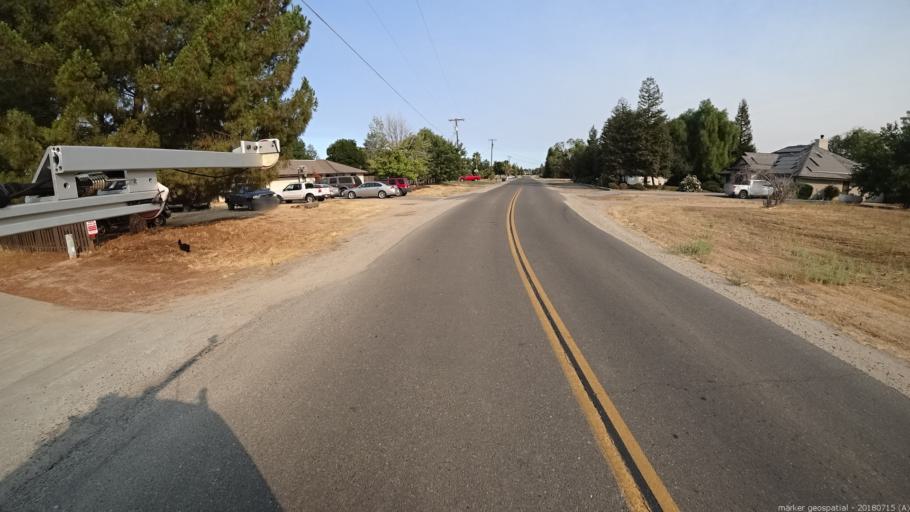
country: US
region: California
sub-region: Madera County
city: Madera Acres
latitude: 37.0126
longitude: -120.0611
